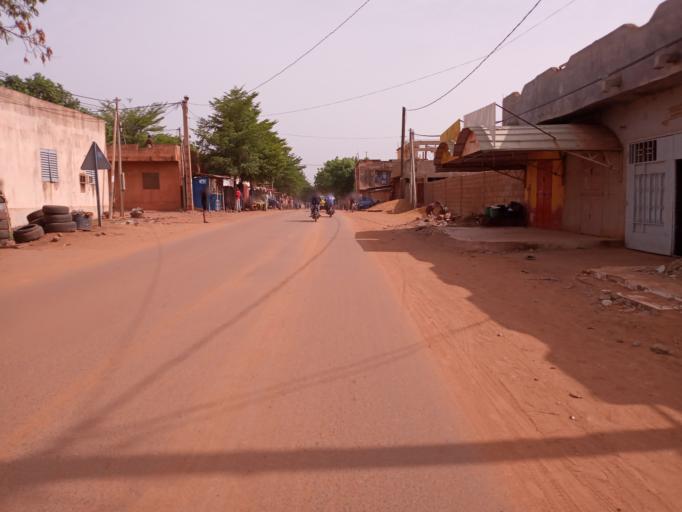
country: ML
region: Bamako
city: Bamako
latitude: 12.6088
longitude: -7.9524
